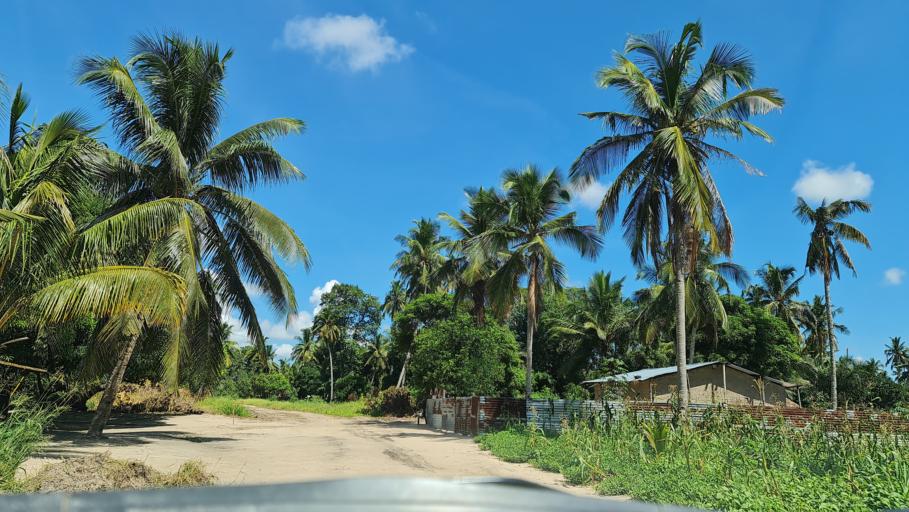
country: MZ
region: Zambezia
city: Quelimane
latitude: -17.3837
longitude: 37.5230
